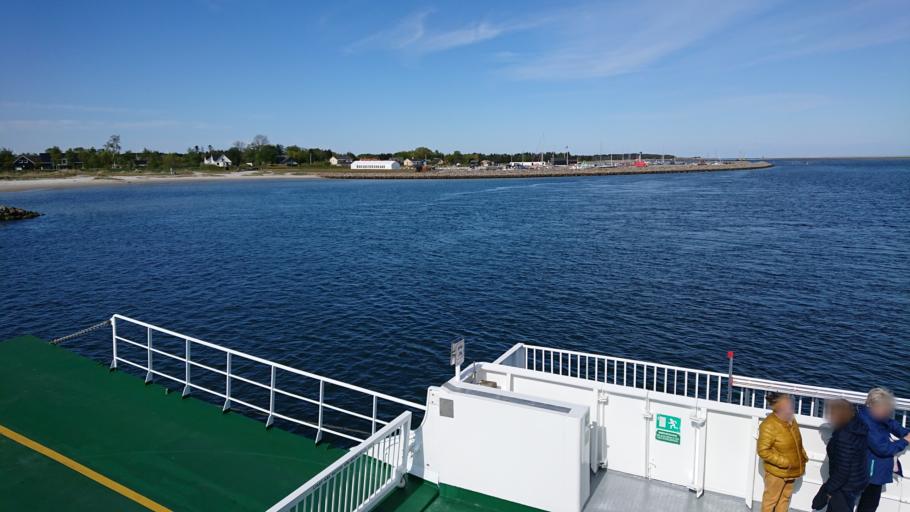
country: DK
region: Central Jutland
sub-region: Norddjurs Kommune
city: Allingabro
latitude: 56.6085
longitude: 10.3009
